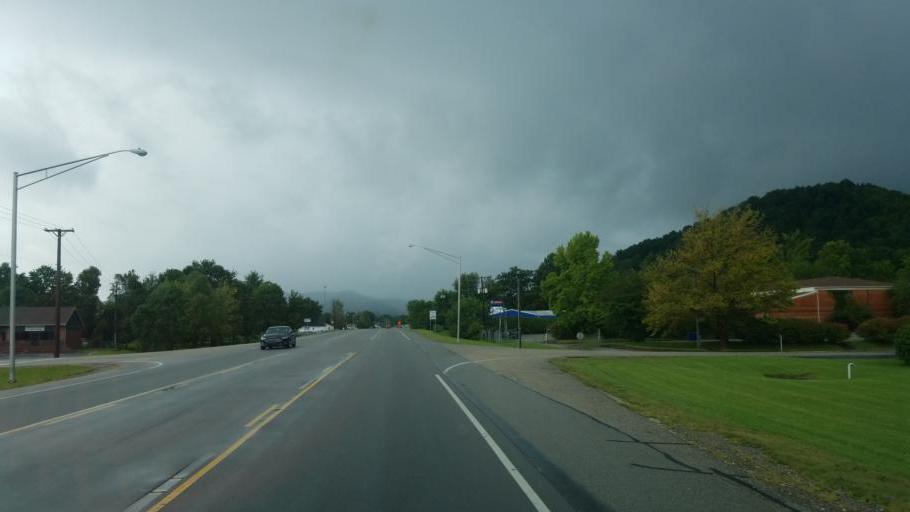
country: US
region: Kentucky
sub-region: Rowan County
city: Morehead
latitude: 38.1756
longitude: -83.4364
